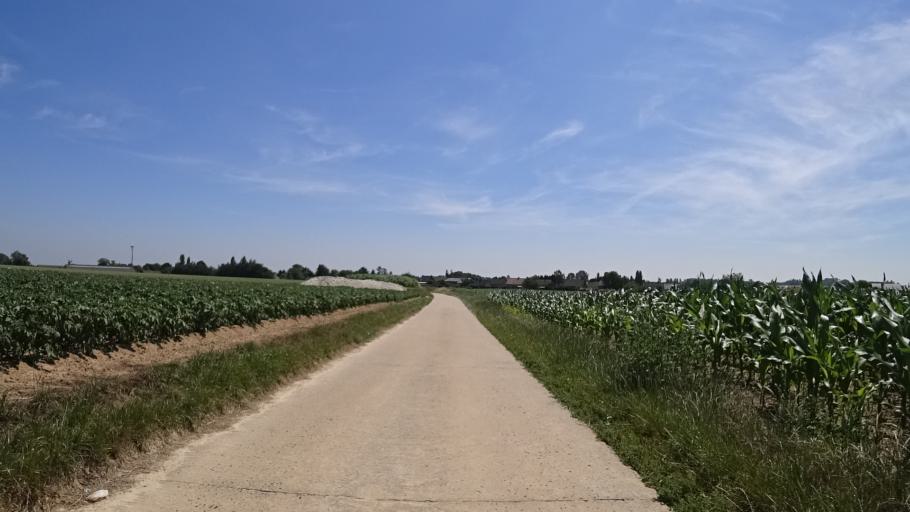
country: BE
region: Wallonia
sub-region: Province du Brabant Wallon
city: Chastre-Villeroux-Blanmont
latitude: 50.5981
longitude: 4.6663
